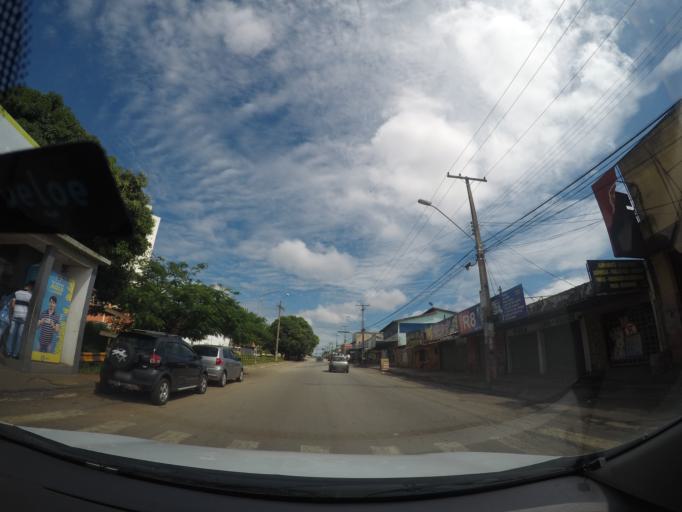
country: BR
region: Goias
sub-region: Goiania
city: Goiania
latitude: -16.6588
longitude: -49.3268
